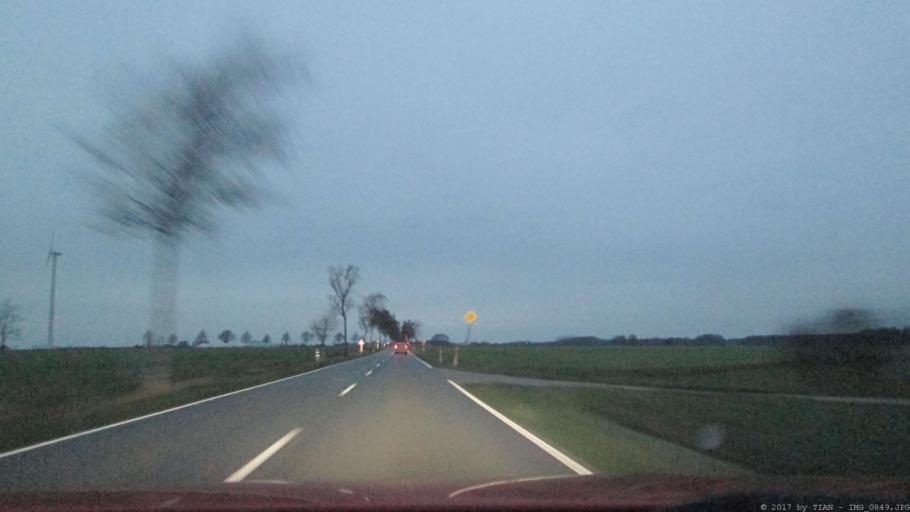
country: DE
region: Lower Saxony
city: Wittingen
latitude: 52.7487
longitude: 10.7282
